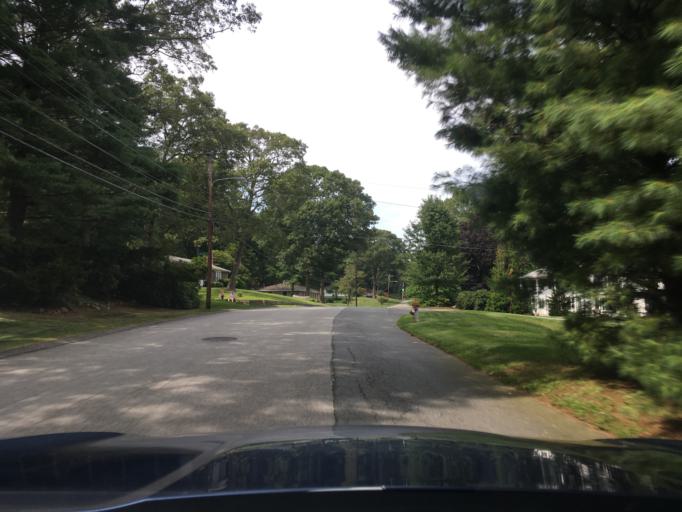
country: US
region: Rhode Island
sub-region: Kent County
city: East Greenwich
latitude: 41.6437
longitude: -71.4800
